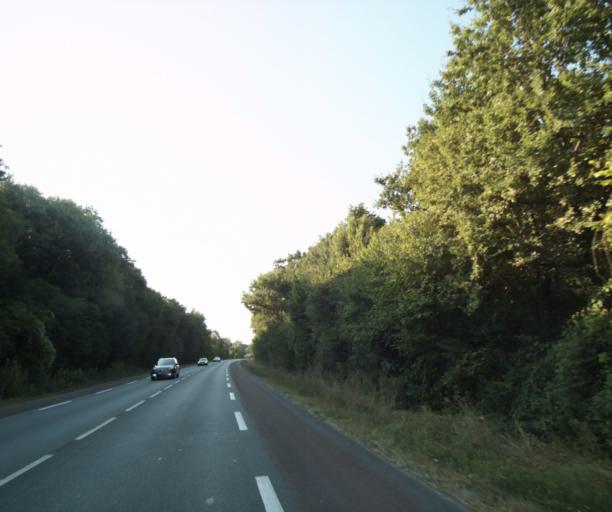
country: FR
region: Poitou-Charentes
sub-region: Departement de la Charente-Maritime
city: Cabariot
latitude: 45.9473
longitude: -0.8663
